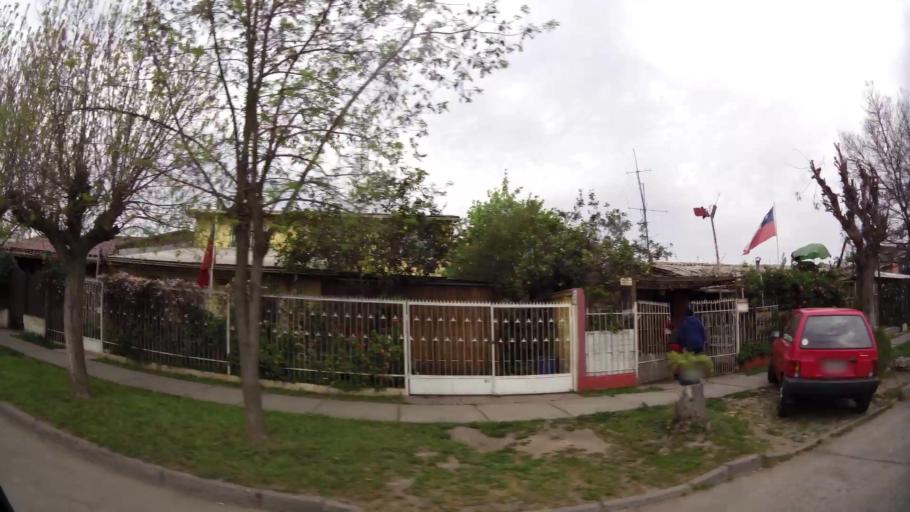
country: CL
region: Santiago Metropolitan
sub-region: Provincia de Santiago
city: Lo Prado
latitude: -33.4993
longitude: -70.7716
